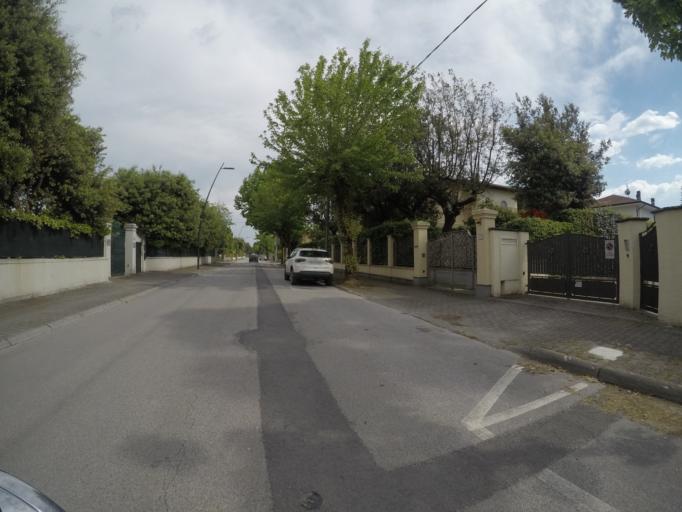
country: IT
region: Tuscany
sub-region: Provincia di Lucca
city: Forte dei Marmi
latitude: 43.9660
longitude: 10.1611
